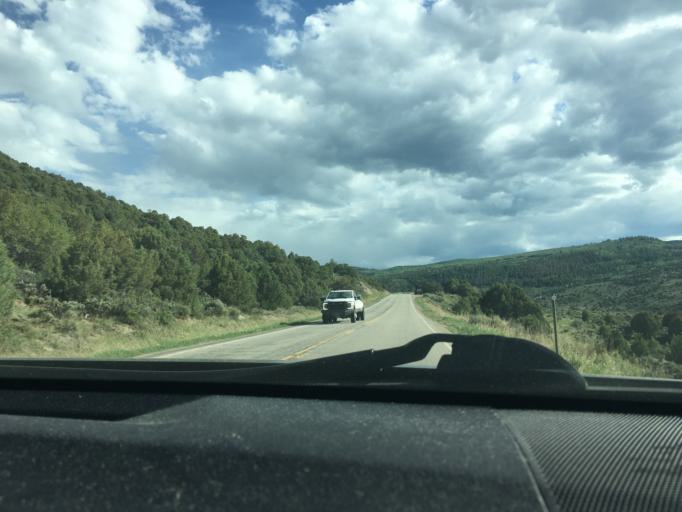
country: US
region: Colorado
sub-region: Eagle County
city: Edwards
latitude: 39.7125
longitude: -106.6844
